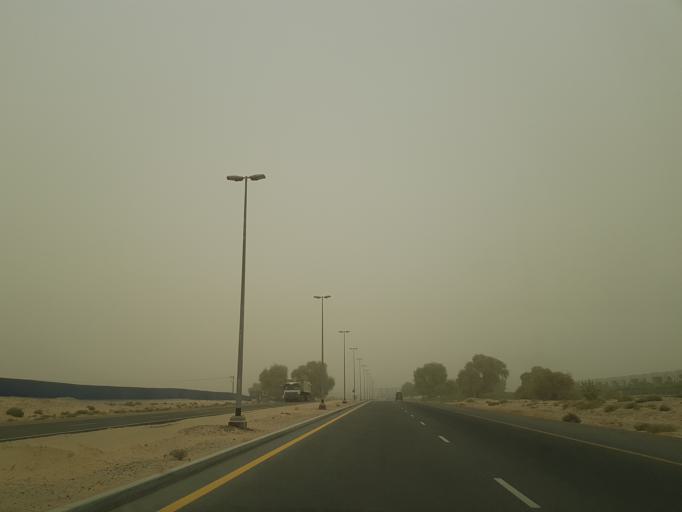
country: AE
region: Dubai
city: Dubai
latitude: 25.1420
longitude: 55.2888
